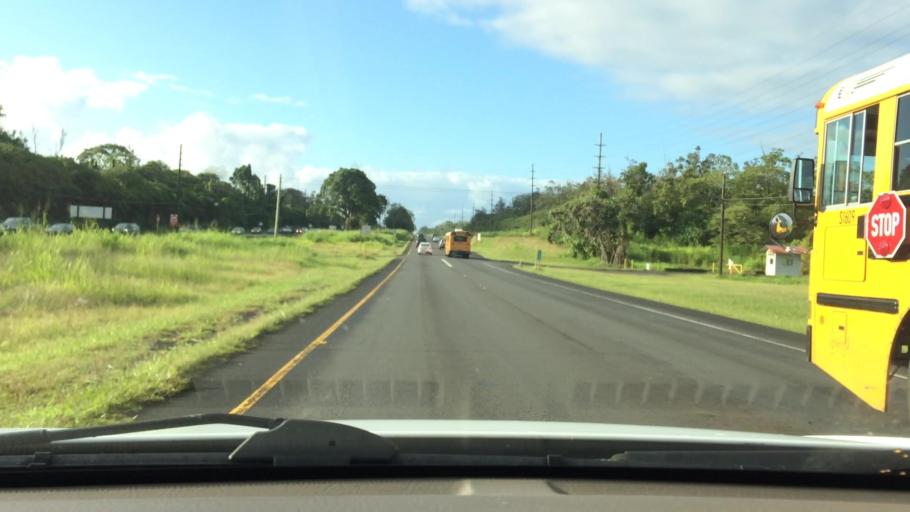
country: US
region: Hawaii
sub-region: Hawaii County
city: Kea'au
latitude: 19.6595
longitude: -155.0580
